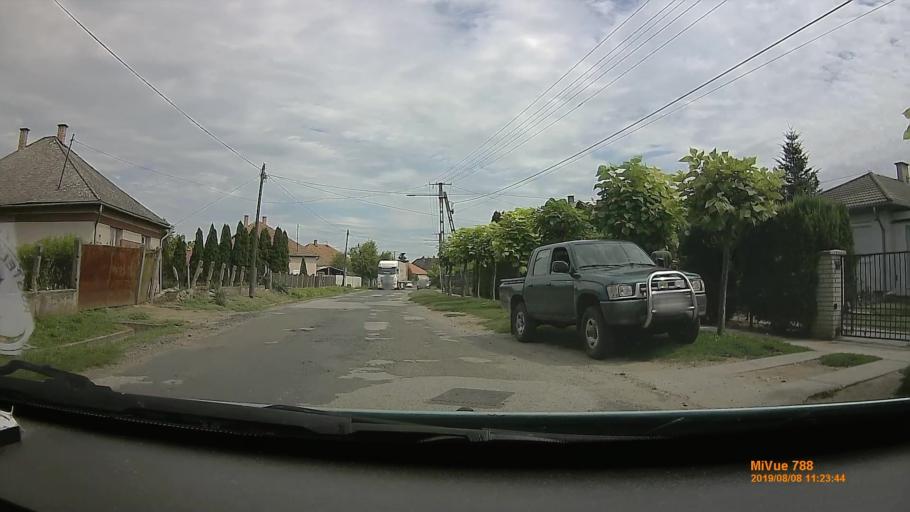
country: HU
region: Szabolcs-Szatmar-Bereg
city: Balkany
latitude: 47.7692
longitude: 21.8511
